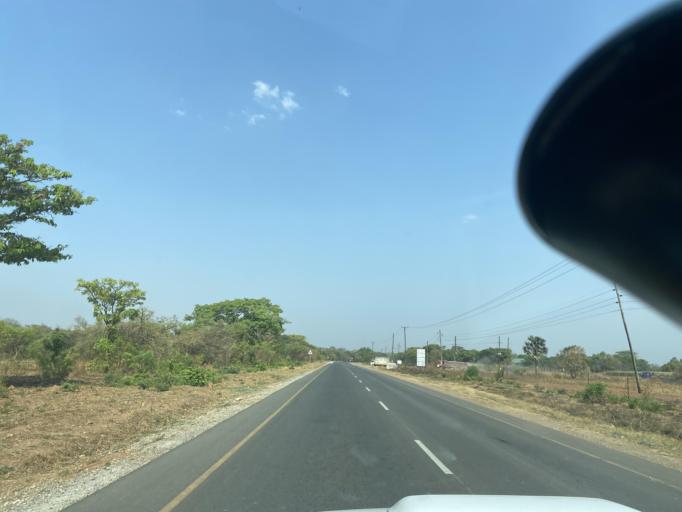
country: ZM
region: Lusaka
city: Lusaka
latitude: -15.3508
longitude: 28.1066
